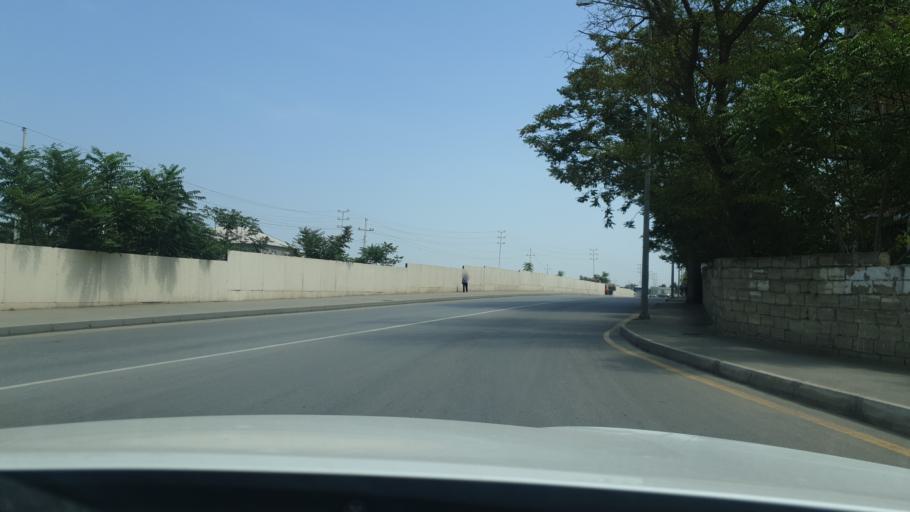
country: AZ
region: Baki
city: Qaracuxur
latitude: 40.3930
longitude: 49.9767
